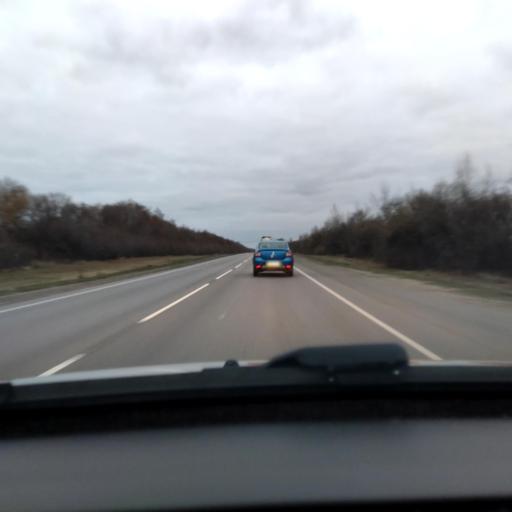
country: RU
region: Lipetsk
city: Borinskoye
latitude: 52.4272
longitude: 39.2622
